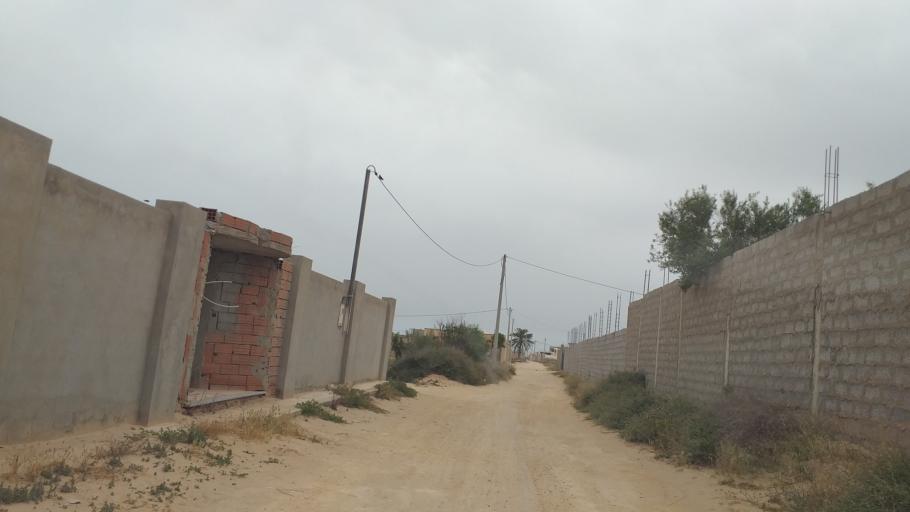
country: TN
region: Qabis
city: Gabes
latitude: 33.9554
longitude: 10.0619
